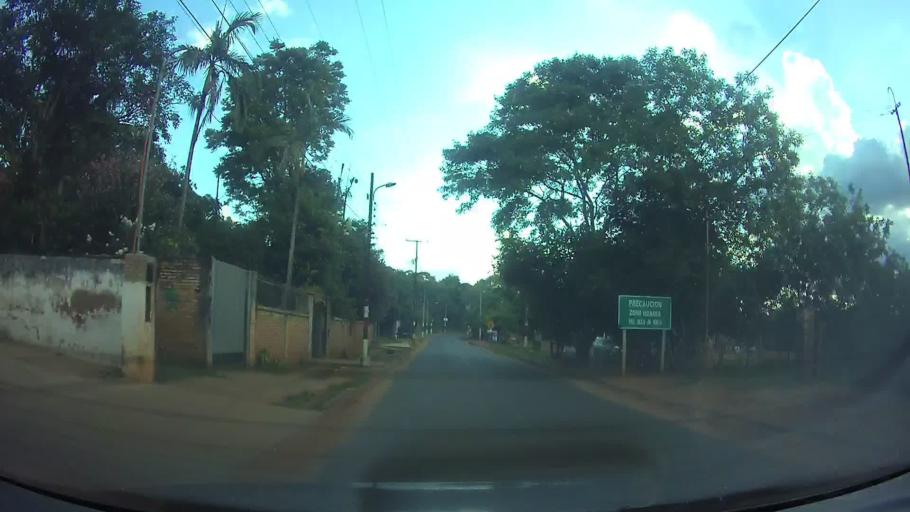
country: PY
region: Central
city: Aregua
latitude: -25.2818
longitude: -57.4345
